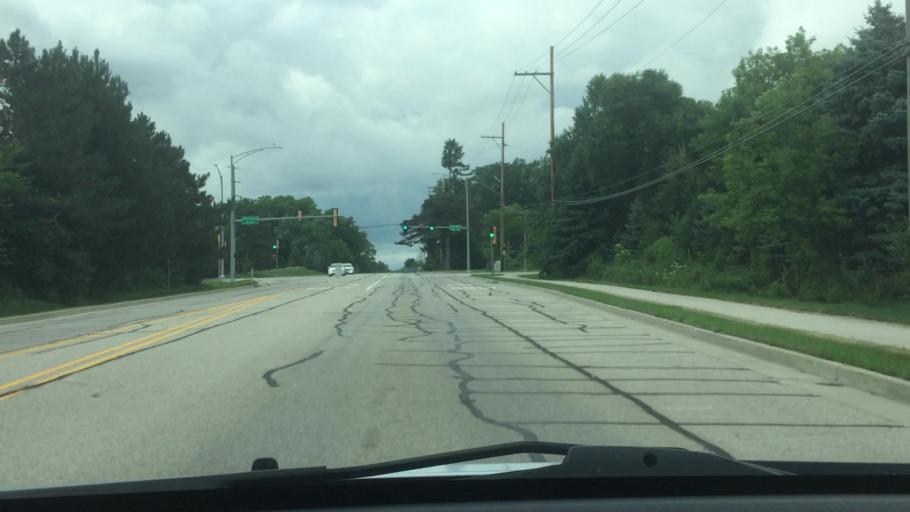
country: US
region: Illinois
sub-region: McHenry County
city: Crystal Lake
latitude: 42.2752
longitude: -88.3208
